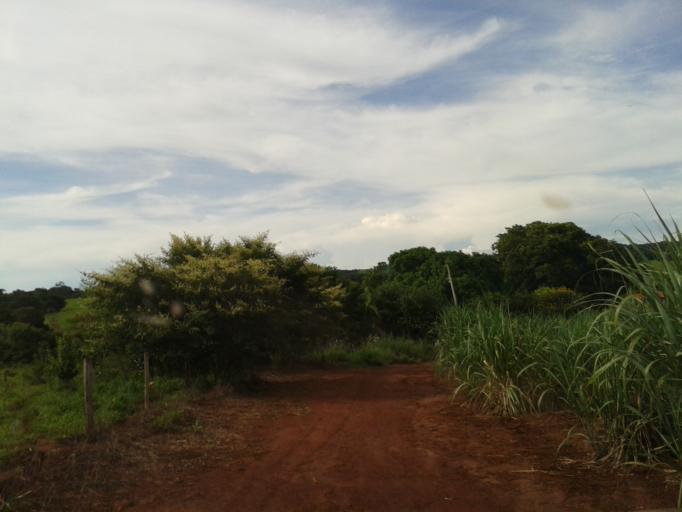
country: BR
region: Minas Gerais
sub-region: Capinopolis
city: Capinopolis
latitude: -18.7912
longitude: -49.8292
